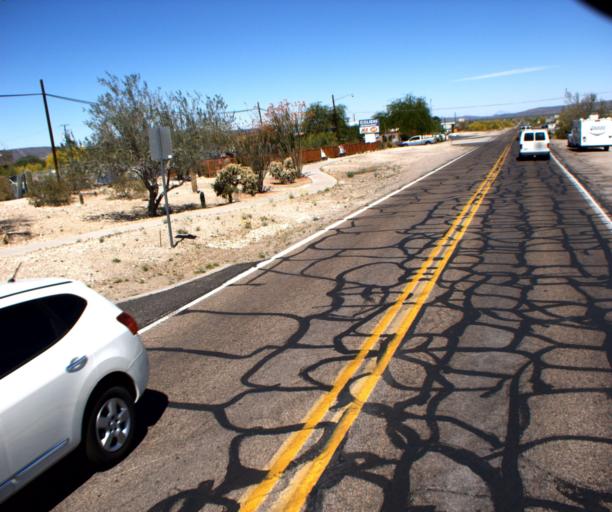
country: US
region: Arizona
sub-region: Pima County
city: Ajo
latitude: 32.3920
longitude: -112.8722
